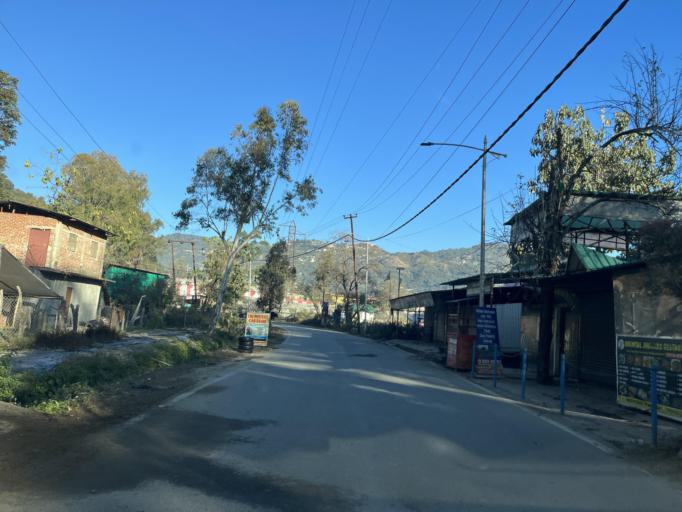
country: IN
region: Uttarakhand
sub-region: Naini Tal
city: Bhim Tal
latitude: 29.3514
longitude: 79.5525
